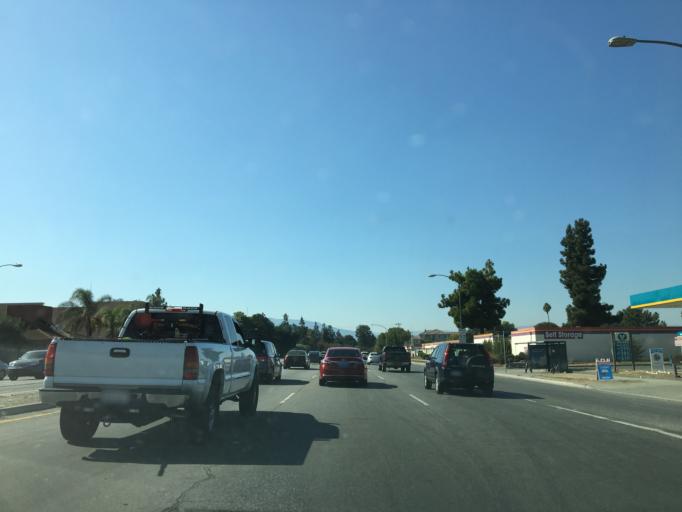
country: US
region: California
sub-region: Santa Clara County
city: Seven Trees
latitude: 37.2770
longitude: -121.8421
